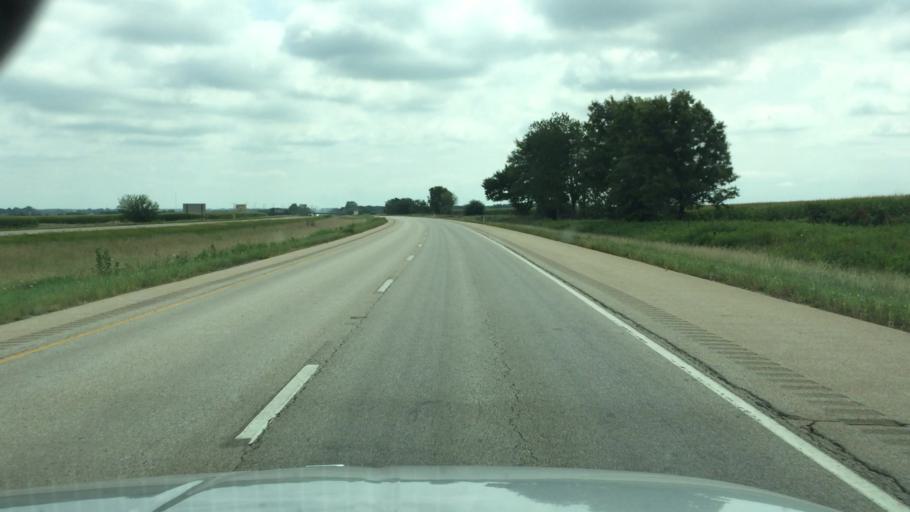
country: US
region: Illinois
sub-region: Knox County
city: Knoxville
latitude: 40.9030
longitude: -90.2289
